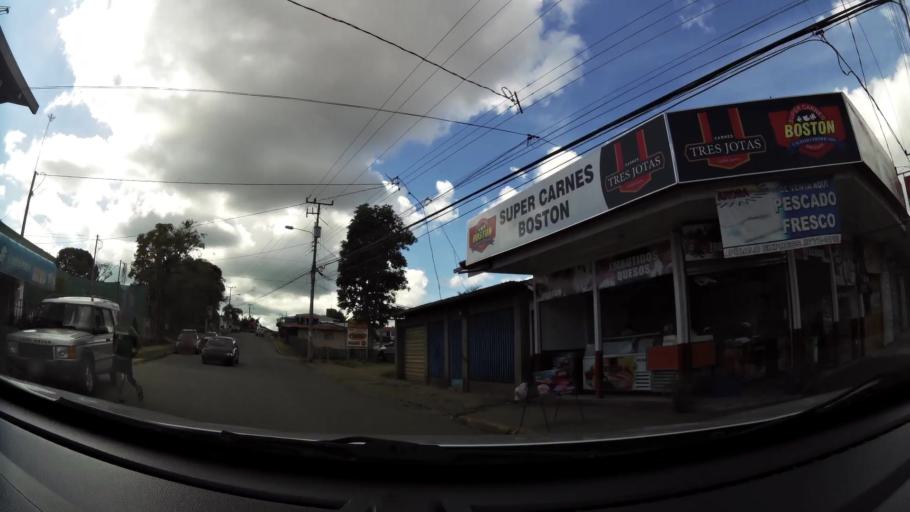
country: CR
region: San Jose
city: San Isidro
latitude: 9.3776
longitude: -83.7067
